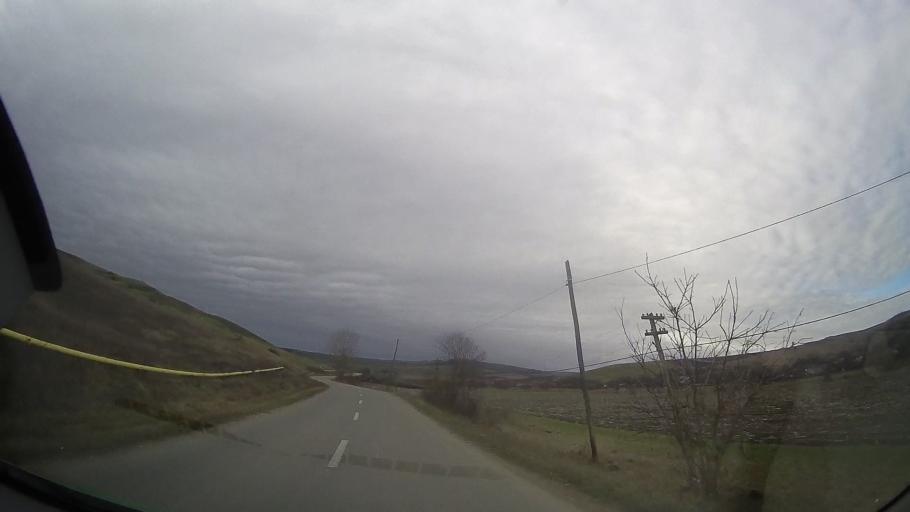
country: RO
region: Cluj
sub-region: Comuna Catina
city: Catina
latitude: 46.8498
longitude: 24.1441
